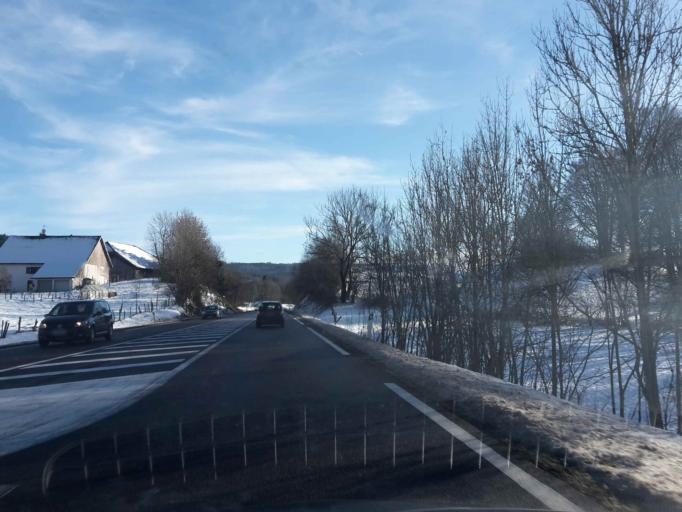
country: FR
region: Franche-Comte
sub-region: Departement du Doubs
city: Valdahon
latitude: 47.0596
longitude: 6.3474
